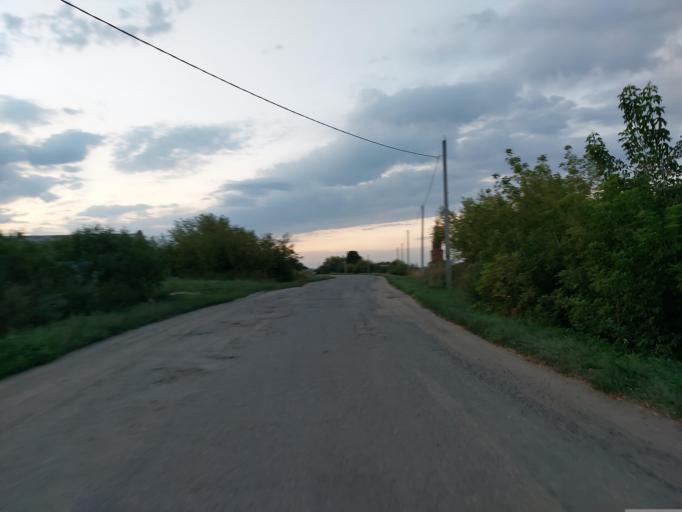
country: RU
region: Lipetsk
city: Dolgorukovo
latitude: 52.3738
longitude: 38.0534
